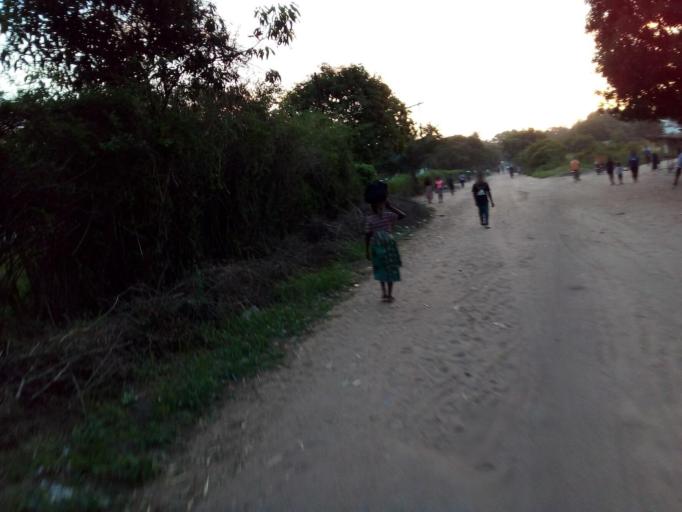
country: MZ
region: Zambezia
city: Quelimane
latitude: -17.6047
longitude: 36.8160
